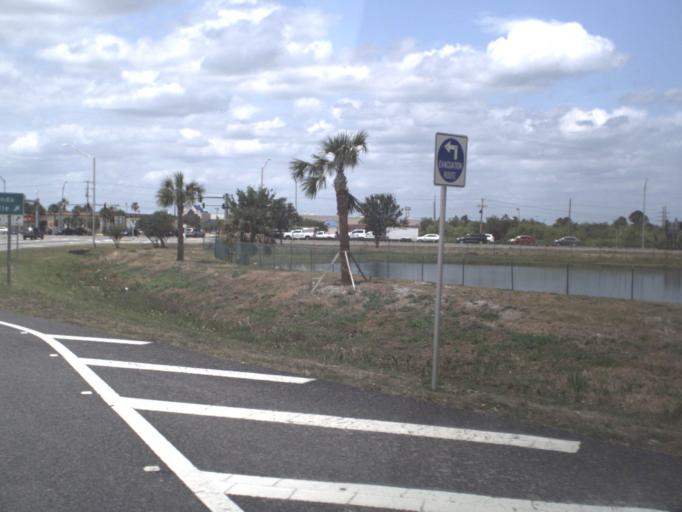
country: US
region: Florida
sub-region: Brevard County
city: Titusville
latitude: 28.5540
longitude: -80.8451
